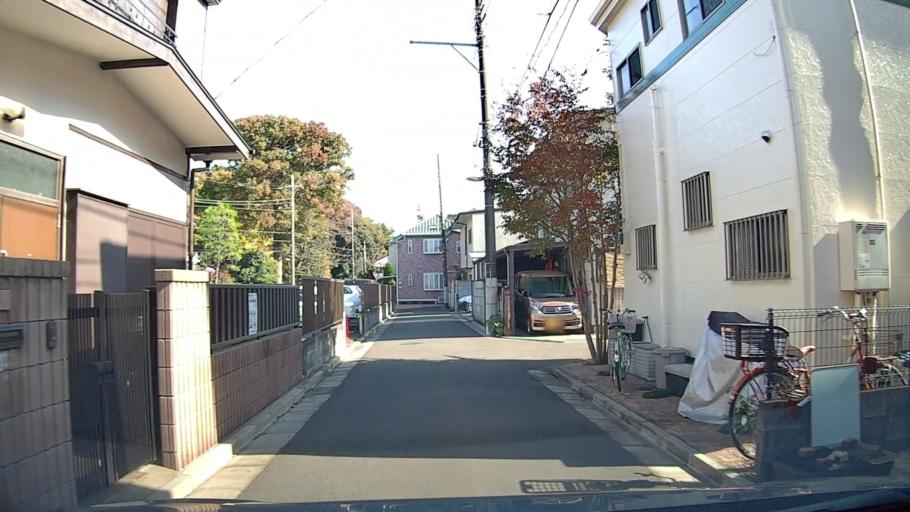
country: JP
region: Tokyo
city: Musashino
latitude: 35.7361
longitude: 139.5949
